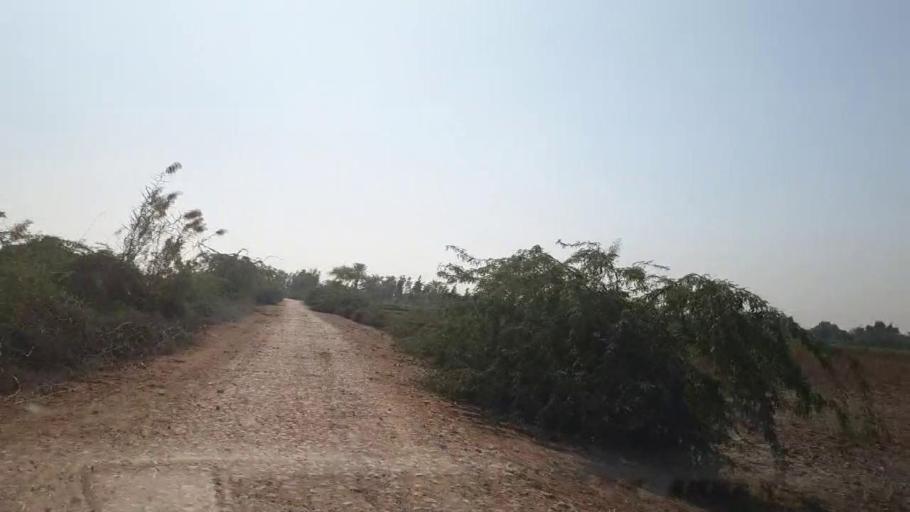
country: PK
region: Sindh
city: Gharo
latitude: 24.6808
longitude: 67.7496
